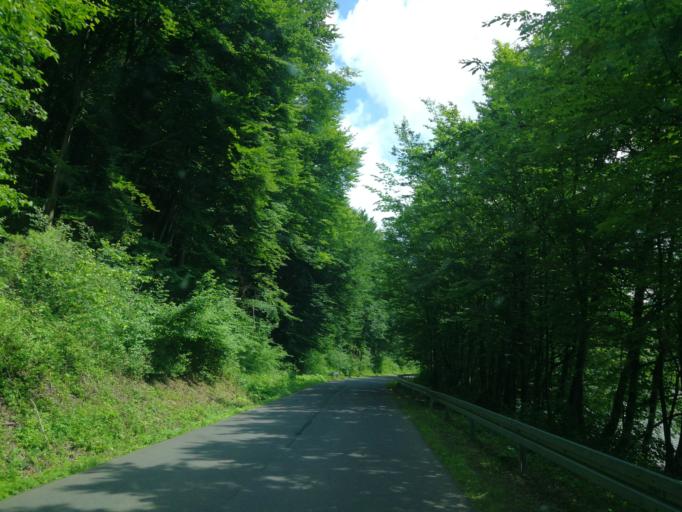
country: PL
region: Subcarpathian Voivodeship
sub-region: Powiat leski
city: Uherce Mineralne
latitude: 49.4254
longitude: 22.4230
